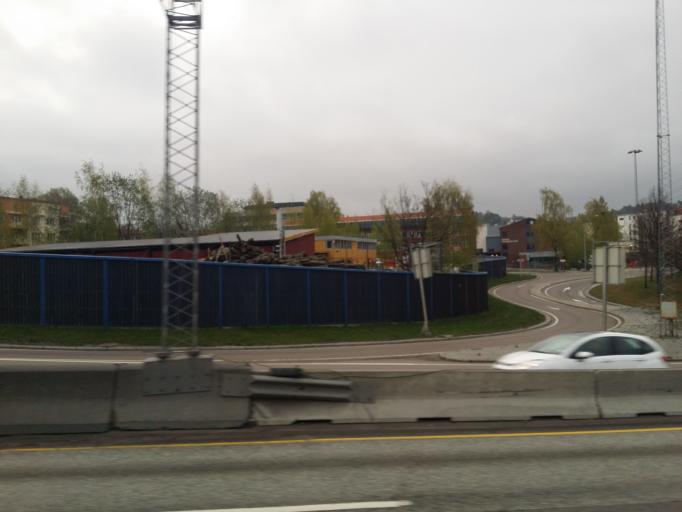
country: NO
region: Oslo
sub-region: Oslo
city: Oslo
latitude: 59.9108
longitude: 10.7935
